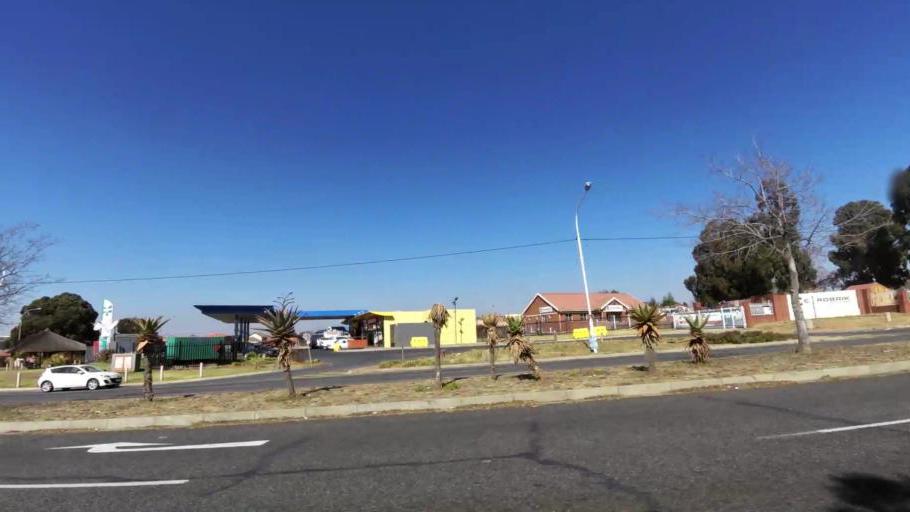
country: ZA
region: Gauteng
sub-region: City of Johannesburg Metropolitan Municipality
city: Johannesburg
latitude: -26.2467
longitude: 27.9847
